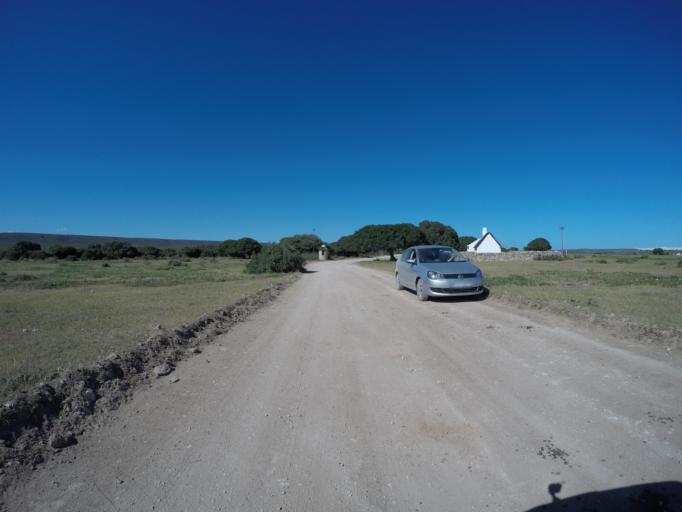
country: ZA
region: Western Cape
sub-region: Overberg District Municipality
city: Bredasdorp
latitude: -34.4535
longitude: 20.4015
